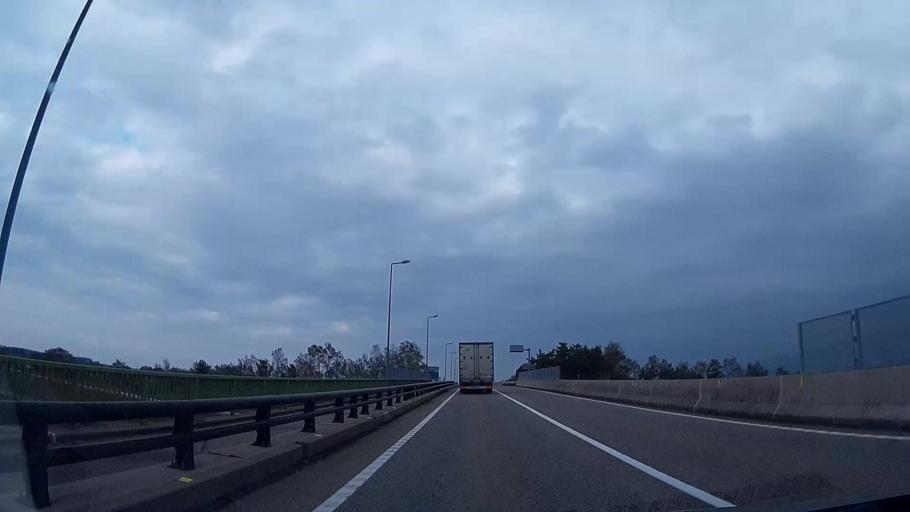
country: JP
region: Toyama
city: Nyuzen
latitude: 36.9021
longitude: 137.4480
